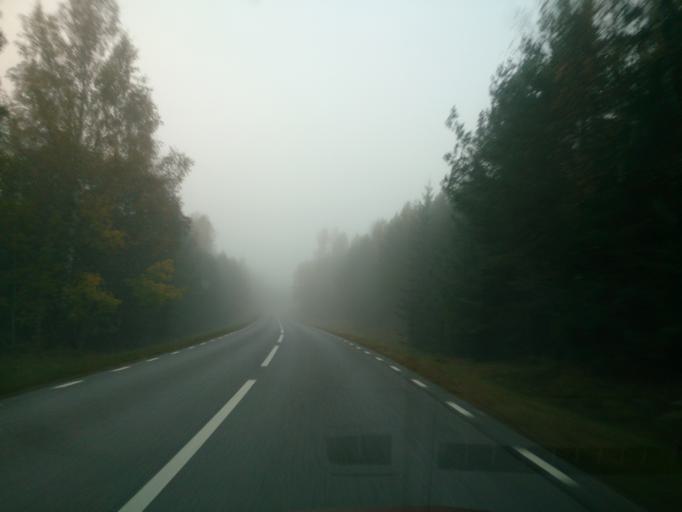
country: SE
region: OEstergoetland
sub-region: Atvidabergs Kommun
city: Atvidaberg
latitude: 58.0939
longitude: 15.9431
